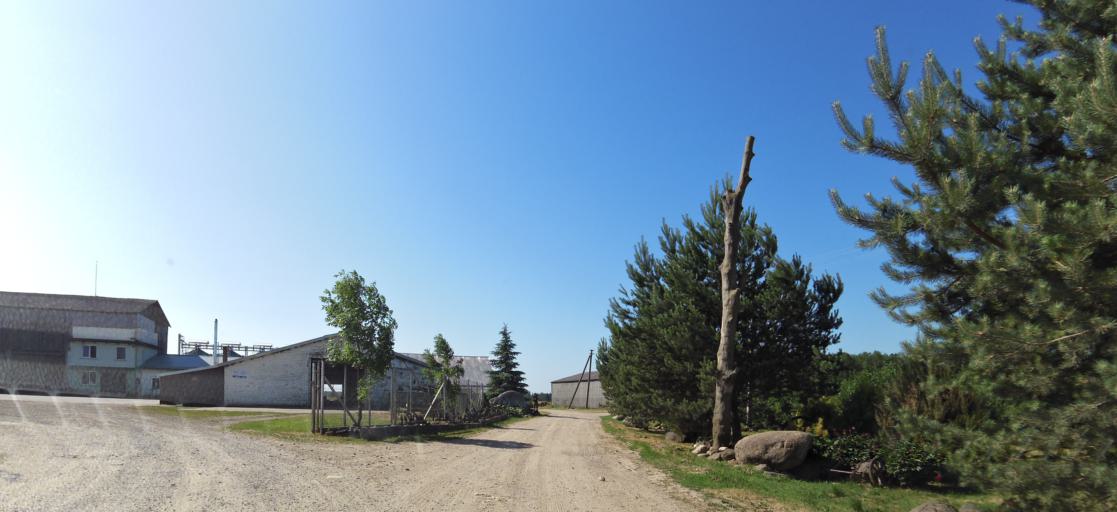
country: LT
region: Panevezys
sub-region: Birzai
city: Birzai
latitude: 56.2446
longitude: 24.8773
